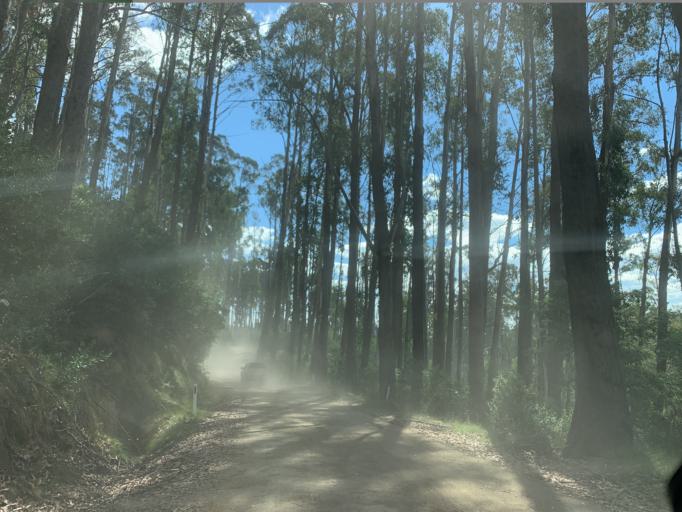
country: AU
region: Victoria
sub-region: Mansfield
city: Mansfield
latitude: -37.0980
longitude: 146.5368
